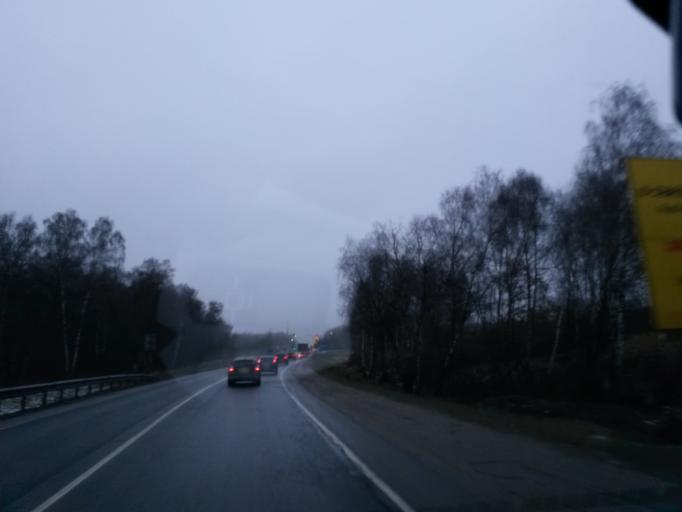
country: RU
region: Moskovskaya
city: Dubrovitsy
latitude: 55.3753
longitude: 37.4007
